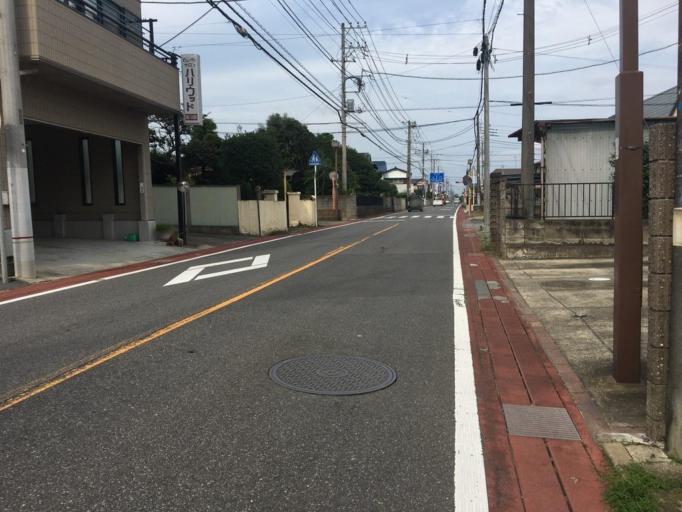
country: JP
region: Chiba
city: Sakura
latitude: 35.7184
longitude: 140.2413
